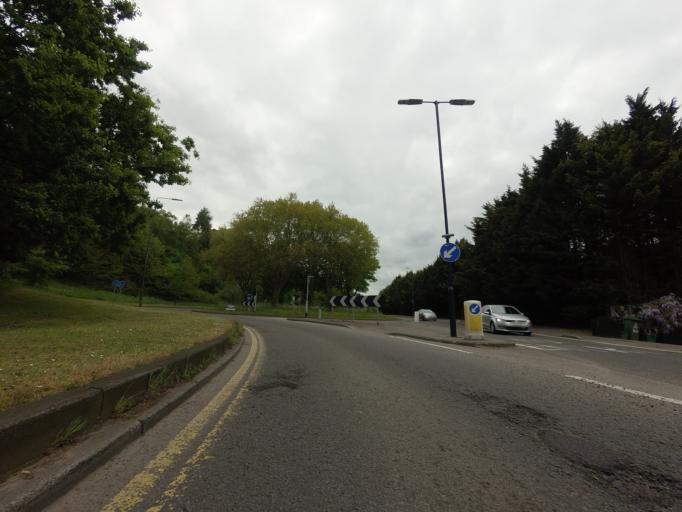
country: GB
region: England
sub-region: Greater London
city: Bexley
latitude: 51.4361
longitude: 0.1483
